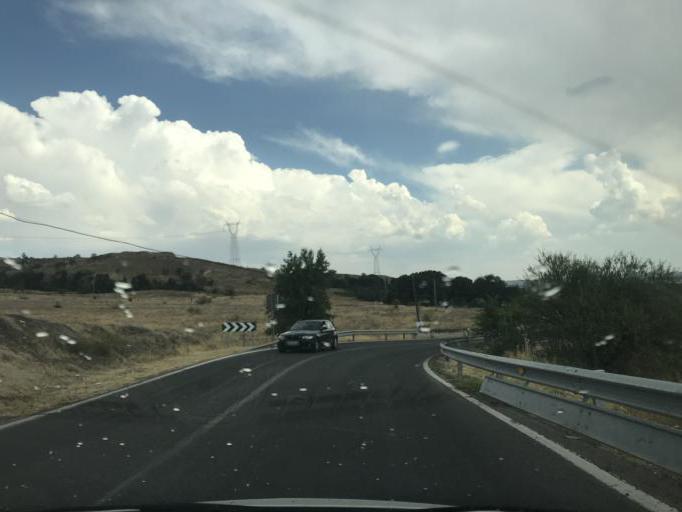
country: ES
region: Madrid
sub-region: Provincia de Madrid
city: Paracuellos de Jarama
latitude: 40.5038
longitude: -3.5404
